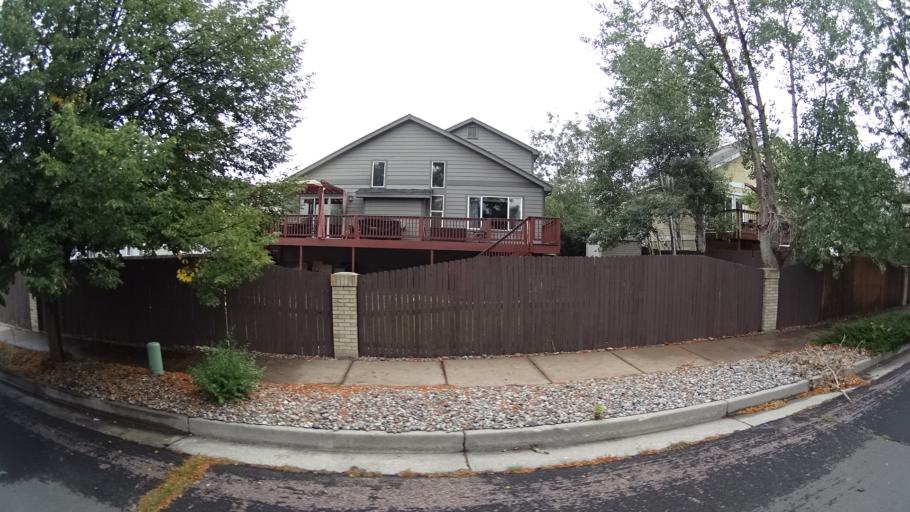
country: US
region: Colorado
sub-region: El Paso County
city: Cimarron Hills
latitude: 38.9284
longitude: -104.7617
